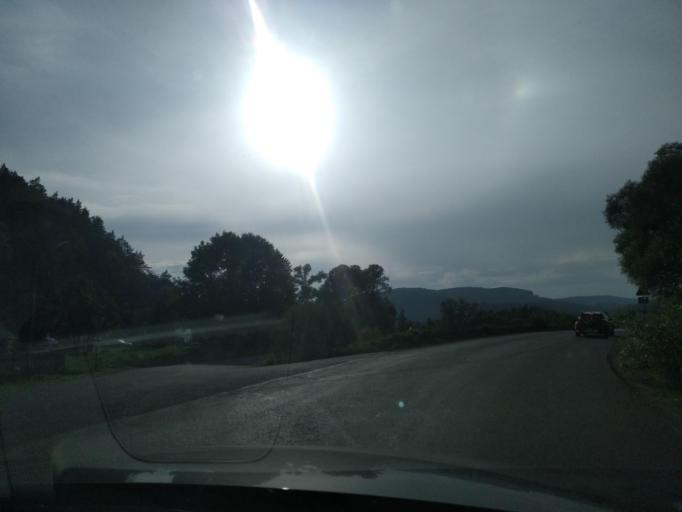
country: PL
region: Subcarpathian Voivodeship
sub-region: Powiat sanocki
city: Sanok
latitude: 49.6131
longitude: 22.2739
